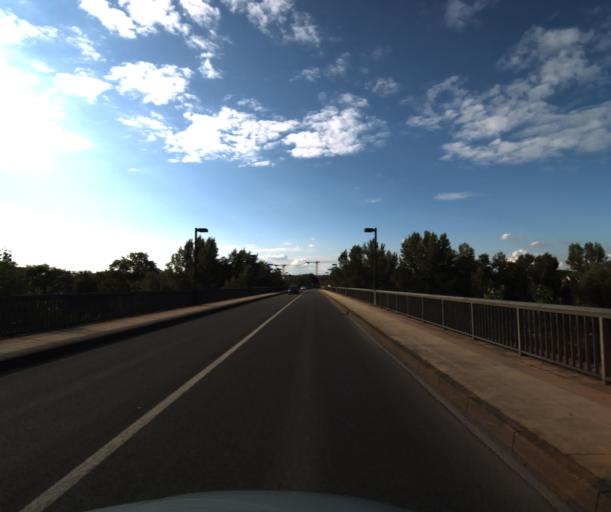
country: FR
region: Midi-Pyrenees
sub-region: Departement de la Haute-Garonne
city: Muret
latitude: 43.4615
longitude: 1.3337
